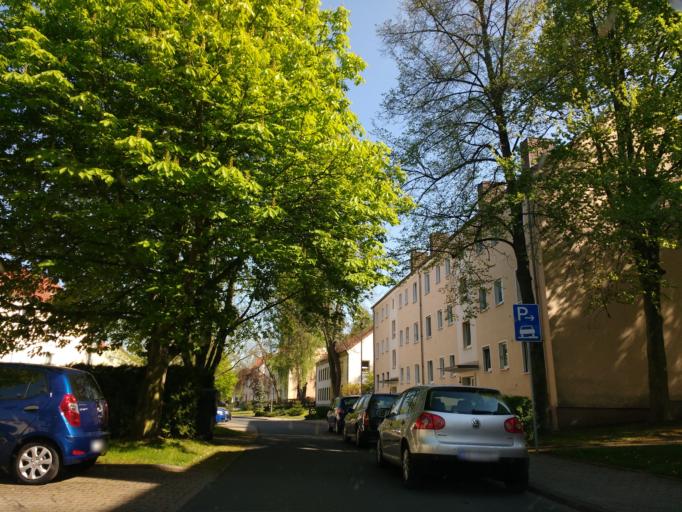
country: DE
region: Saxony-Anhalt
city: Zeitz
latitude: 51.0423
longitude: 12.1312
